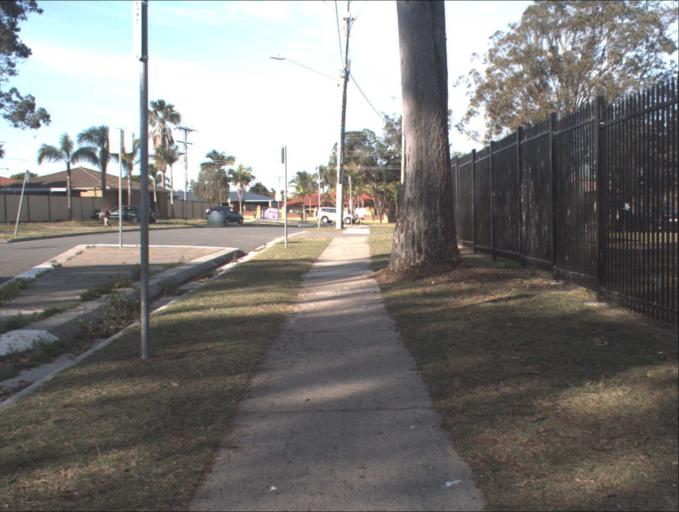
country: AU
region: Queensland
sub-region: Logan
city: Woodridge
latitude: -27.6694
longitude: 153.0548
